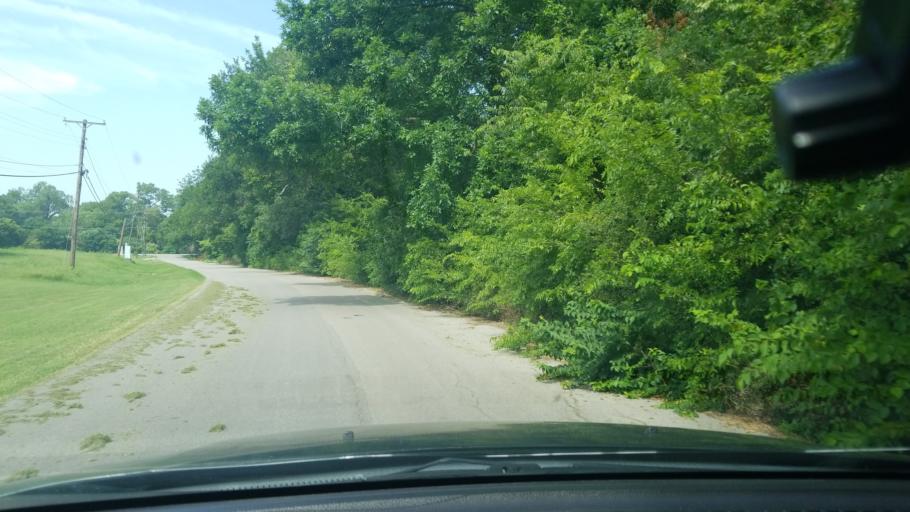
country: US
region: Texas
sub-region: Dallas County
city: Highland Park
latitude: 32.8071
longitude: -96.7165
